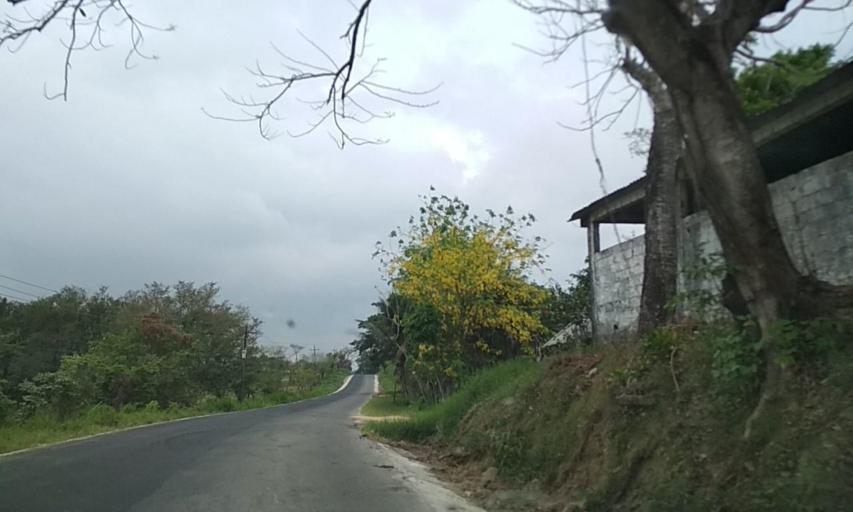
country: MX
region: Tabasco
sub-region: Huimanguillo
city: Francisco Rueda
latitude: 17.7266
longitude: -94.1012
